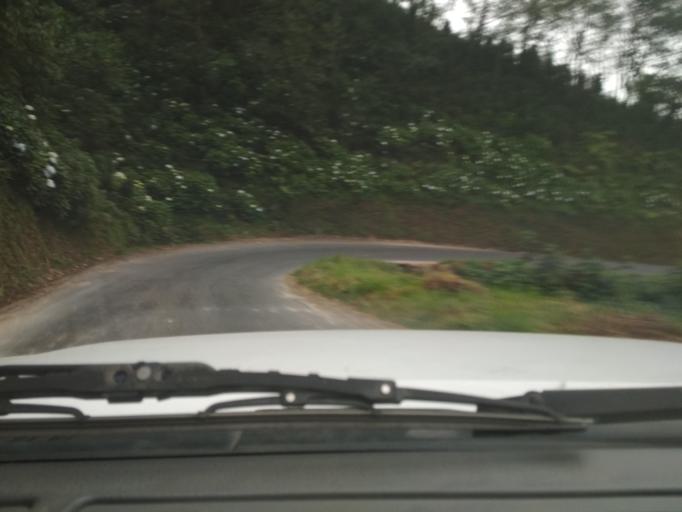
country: MX
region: Veracruz
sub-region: La Perla
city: Metlac Hernandez (Metlac Primero)
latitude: 18.9661
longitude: -97.1476
